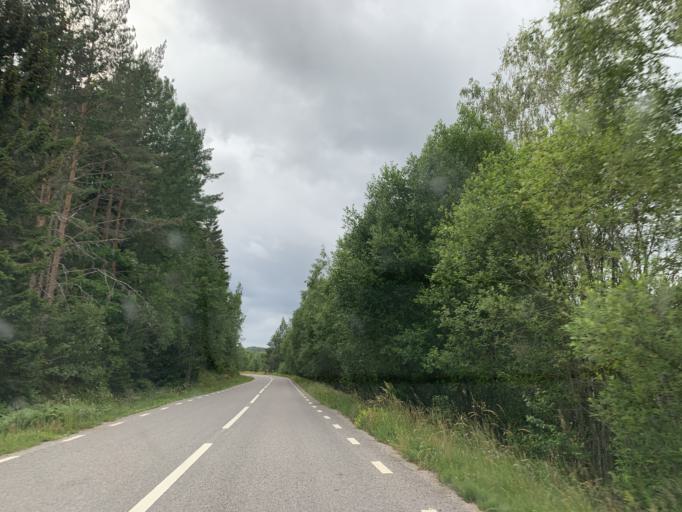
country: SE
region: Kalmar
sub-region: Vasterviks Kommun
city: Overum
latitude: 58.0199
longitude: 16.1437
